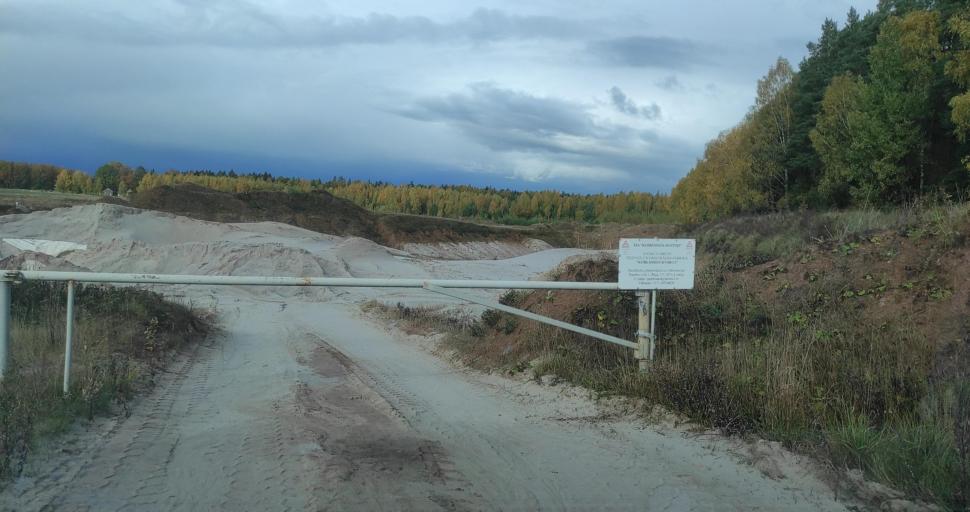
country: LV
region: Skrunda
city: Skrunda
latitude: 56.6035
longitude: 21.9153
